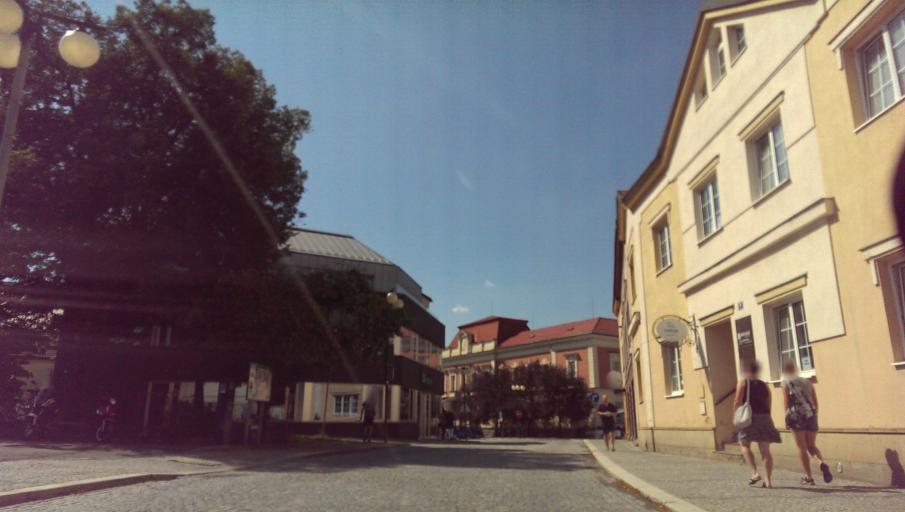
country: CZ
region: Zlin
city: Valasske Mezirici
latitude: 49.4702
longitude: 17.9713
